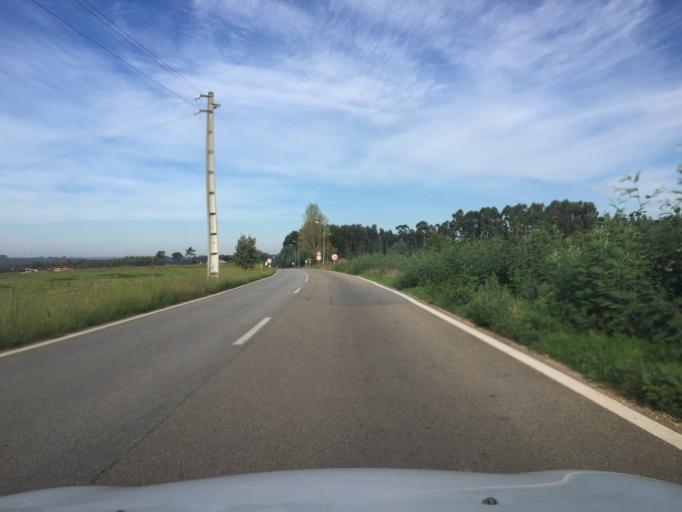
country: PT
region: Aveiro
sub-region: Anadia
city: Anadia
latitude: 40.4494
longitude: -8.4269
